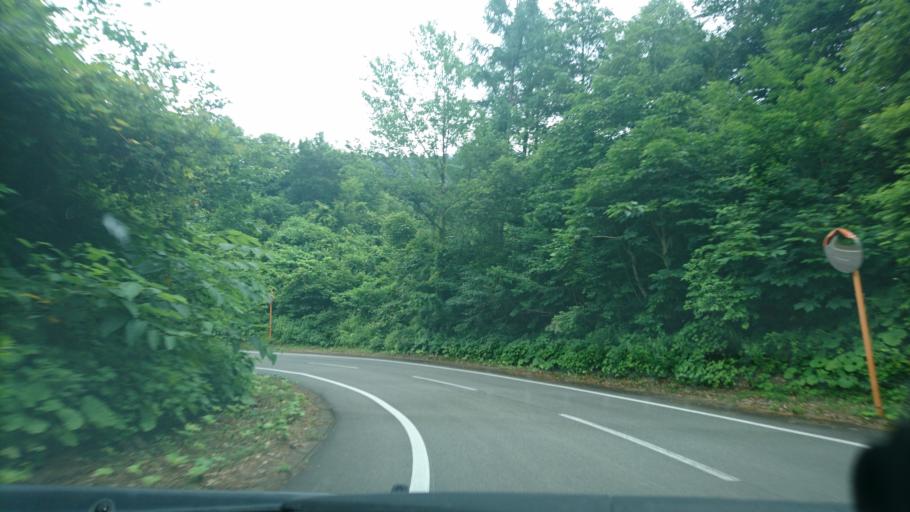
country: JP
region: Akita
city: Yuzawa
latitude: 39.1616
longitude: 140.7505
